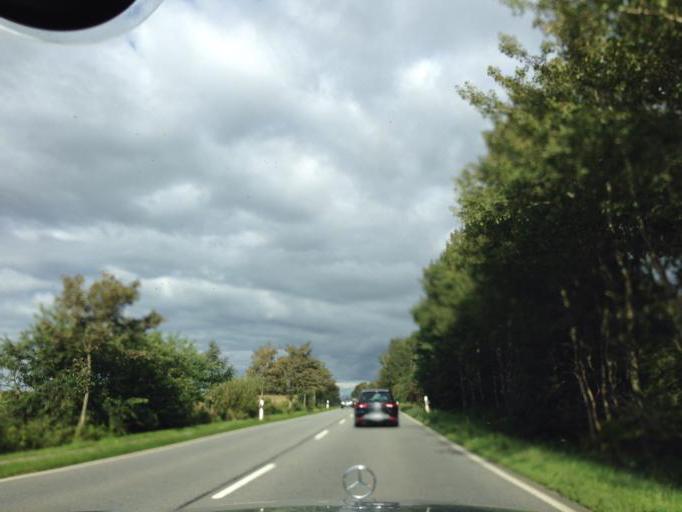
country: DE
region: Schleswig-Holstein
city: Leck
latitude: 54.7437
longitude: 8.9595
